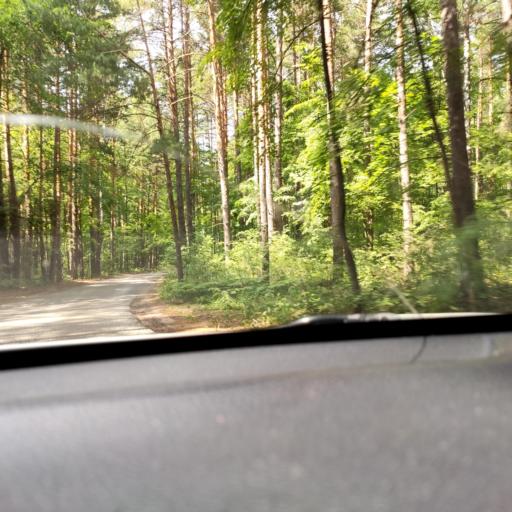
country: RU
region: Tatarstan
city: Verkhniy Uslon
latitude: 55.6525
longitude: 49.0301
